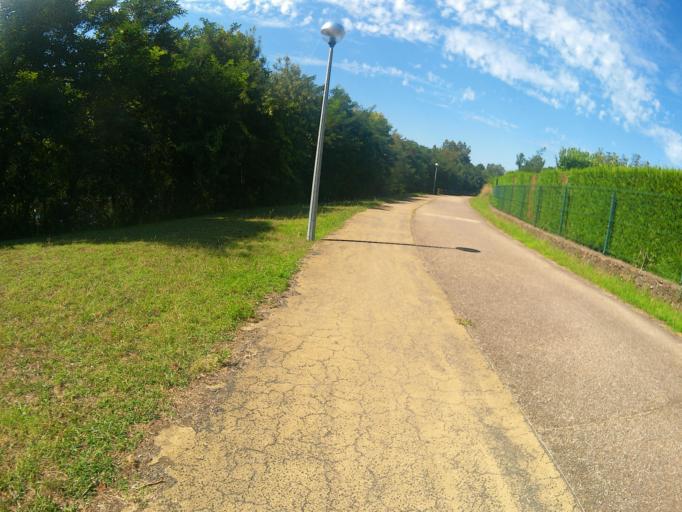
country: PT
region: Viana do Castelo
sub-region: Valenca
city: Valenca
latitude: 42.0141
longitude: -8.6562
